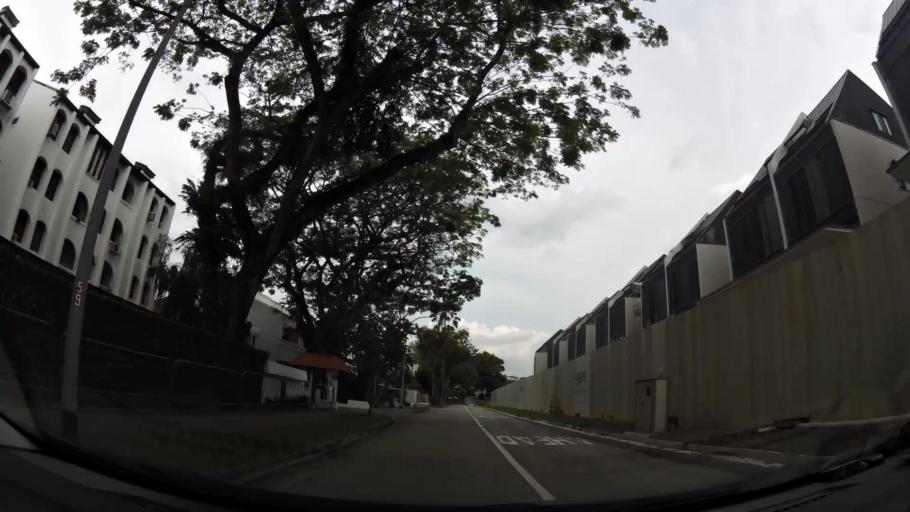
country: SG
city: Singapore
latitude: 1.3227
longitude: 103.8025
